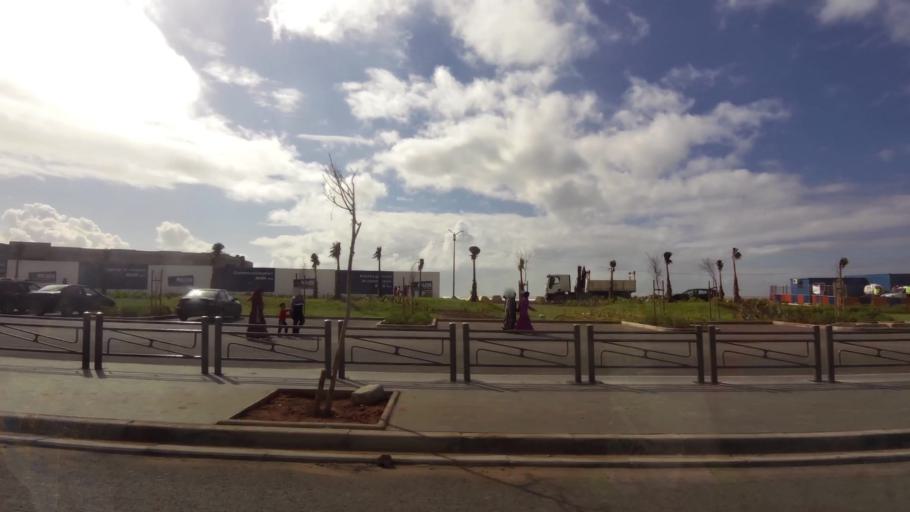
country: MA
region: Grand Casablanca
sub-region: Casablanca
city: Casablanca
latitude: 33.5789
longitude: -7.7039
